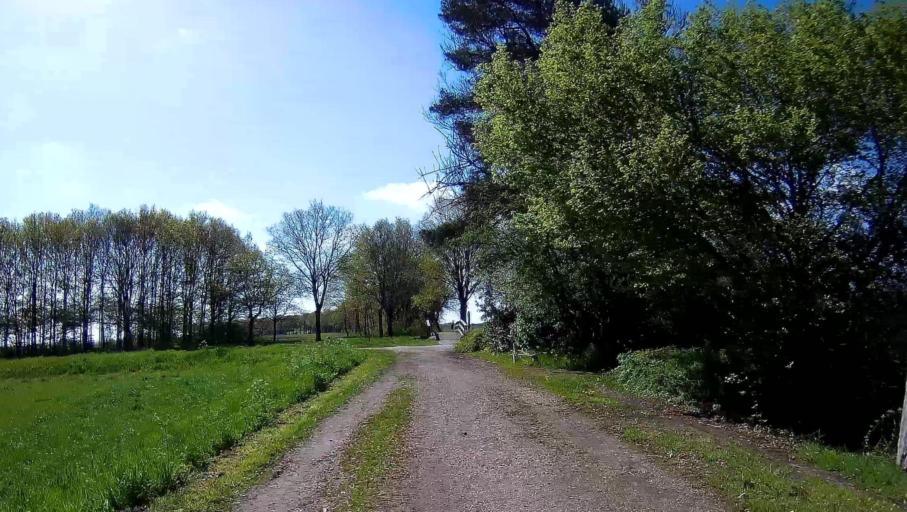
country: NL
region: Drenthe
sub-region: Gemeente Borger-Odoorn
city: Borger
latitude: 52.9472
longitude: 6.8252
